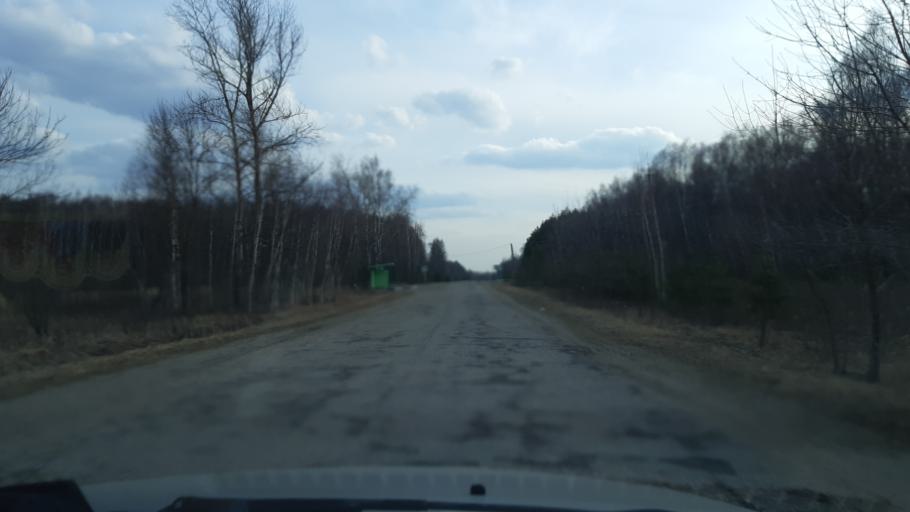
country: RU
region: Vladimir
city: Nikologory
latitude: 56.1197
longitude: 41.9864
